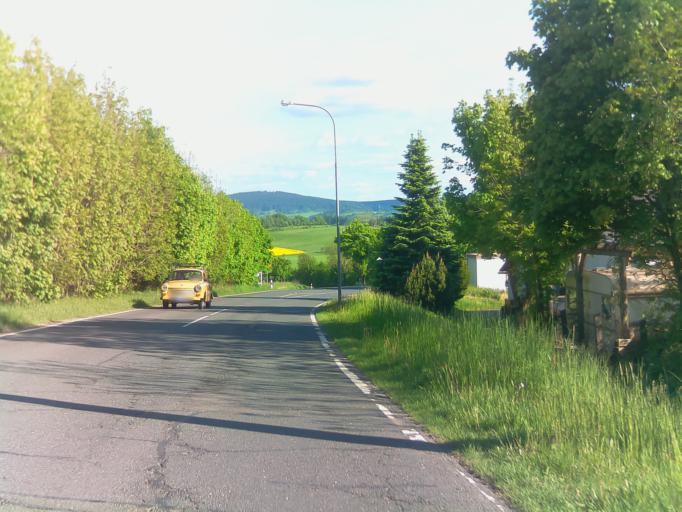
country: DE
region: Thuringia
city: Herschdorf
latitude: 50.6269
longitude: 11.0529
